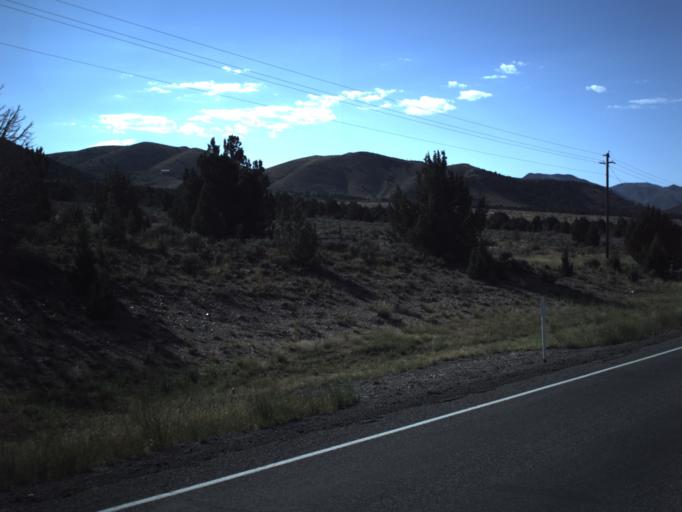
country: US
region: Utah
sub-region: Utah County
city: Genola
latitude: 39.9325
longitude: -112.1492
